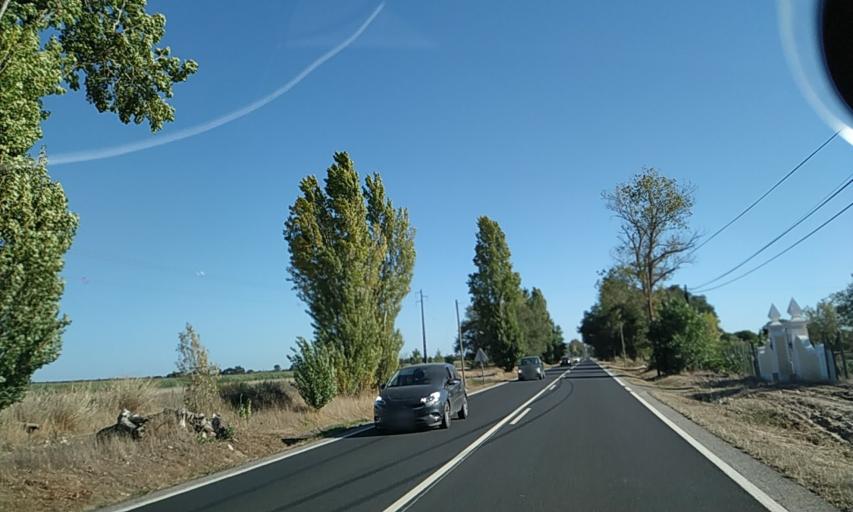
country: PT
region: Santarem
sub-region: Benavente
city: Poceirao
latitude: 38.8110
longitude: -8.8808
